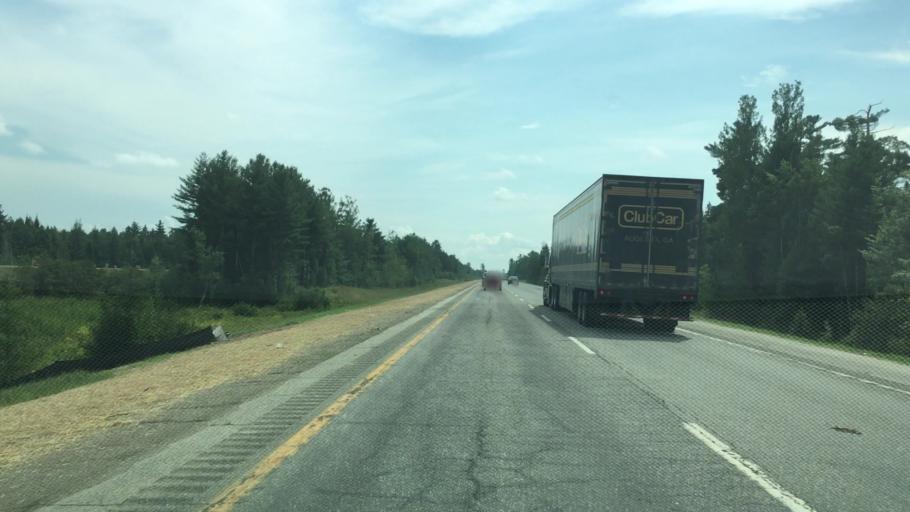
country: US
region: Maine
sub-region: Penobscot County
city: Medway
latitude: 45.5853
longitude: -68.5432
